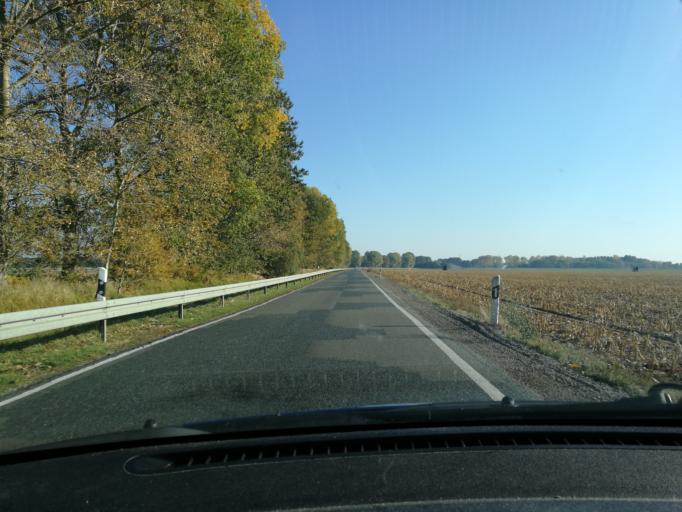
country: DE
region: Mecklenburg-Vorpommern
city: Domitz
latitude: 53.1554
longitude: 11.2477
